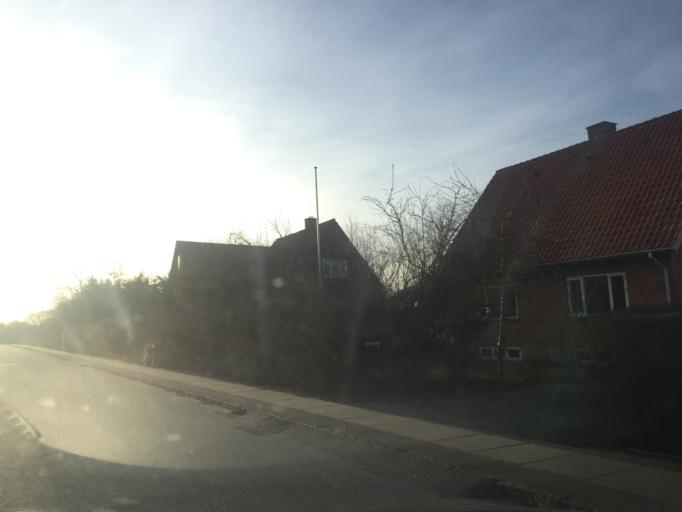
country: DK
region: Capital Region
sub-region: Hoje-Taastrup Kommune
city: Taastrup
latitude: 55.6498
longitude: 12.3096
